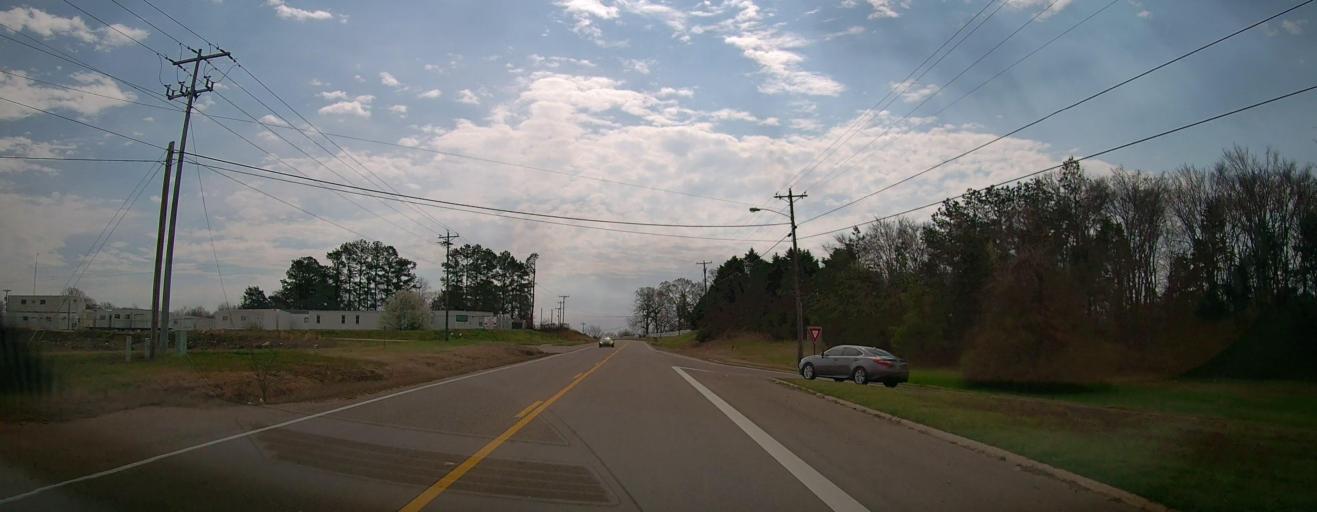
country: US
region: Mississippi
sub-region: De Soto County
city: Olive Branch
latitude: 34.9830
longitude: -89.8583
